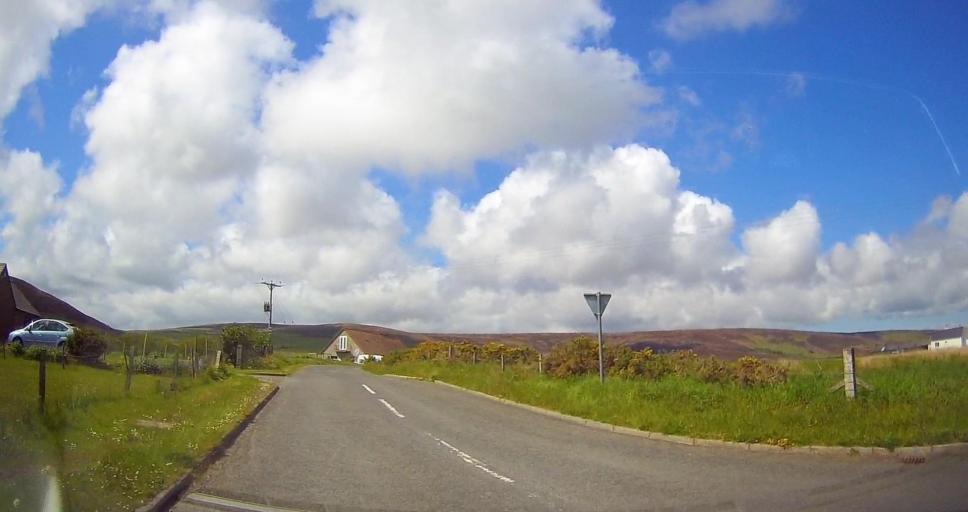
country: GB
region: Scotland
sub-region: Orkney Islands
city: Orkney
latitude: 59.0474
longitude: -3.0826
